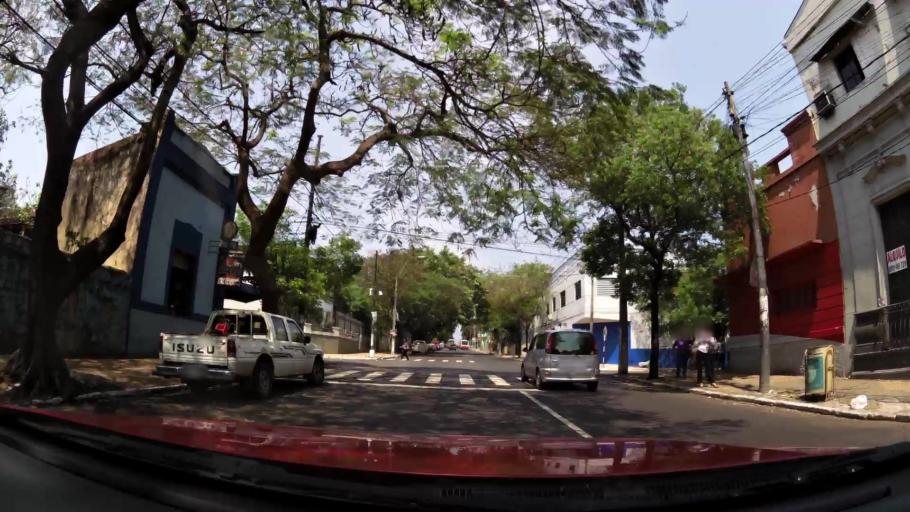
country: PY
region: Asuncion
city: Asuncion
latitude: -25.2852
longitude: -57.6461
